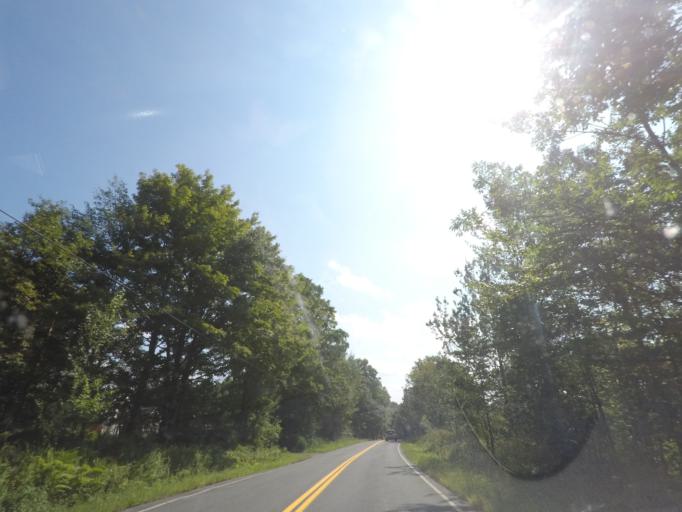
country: US
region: New York
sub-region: Rensselaer County
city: Poestenkill
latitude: 42.7139
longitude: -73.5083
